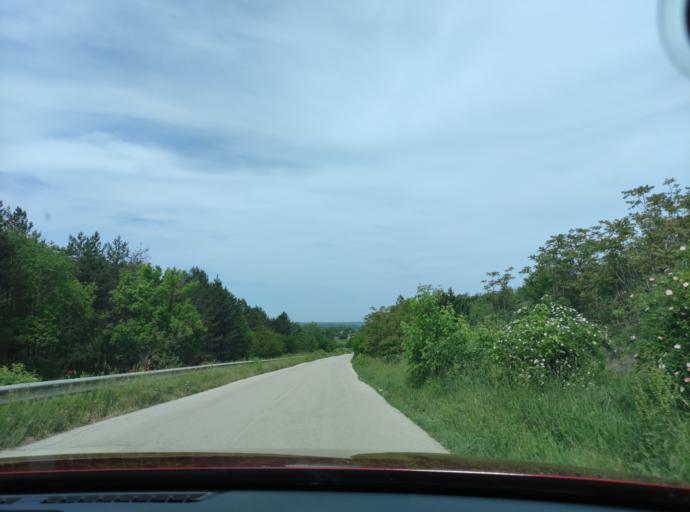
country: BG
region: Pleven
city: Iskur
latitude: 43.5345
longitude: 24.2978
